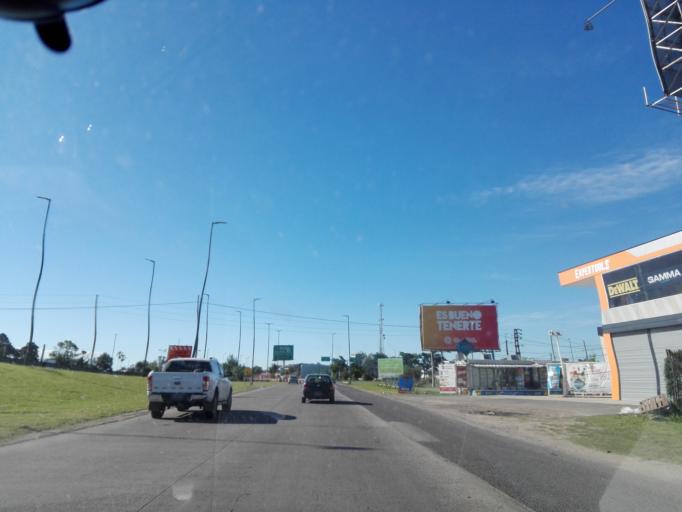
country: AR
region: Buenos Aires
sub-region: Partido de La Plata
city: La Plata
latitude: -34.8949
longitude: -57.9925
